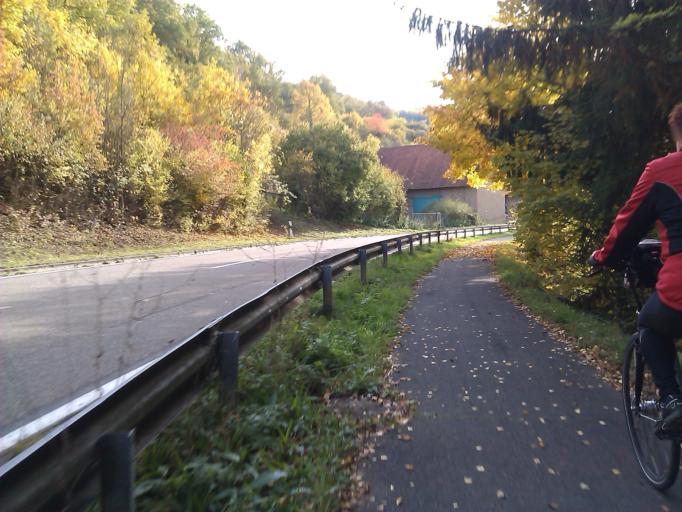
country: DE
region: Rheinland-Pfalz
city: Odenbach
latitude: 49.6805
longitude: 7.6550
